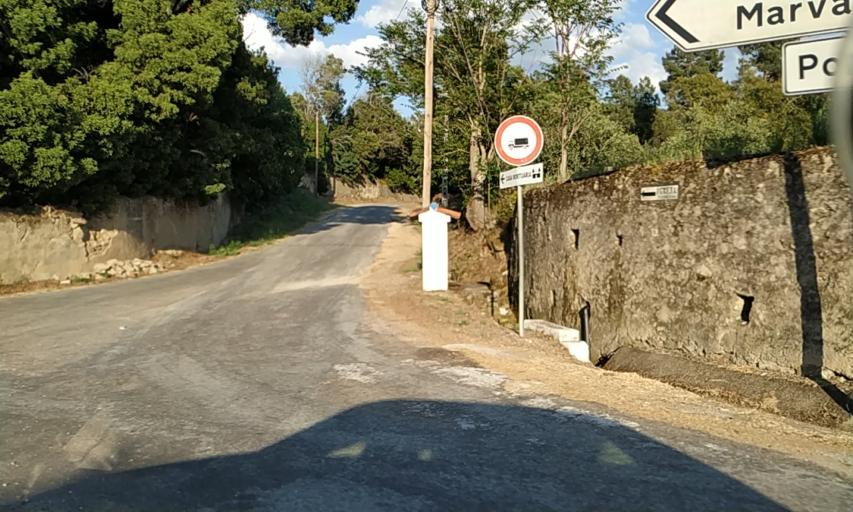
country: PT
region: Portalegre
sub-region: Portalegre
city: Portalegre
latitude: 39.3243
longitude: -7.4361
